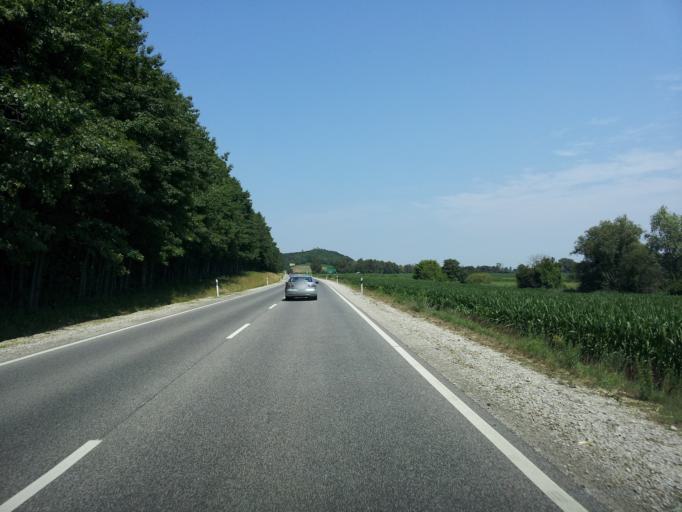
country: HU
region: Zala
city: Zalaegerszeg
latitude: 46.8325
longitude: 16.9289
